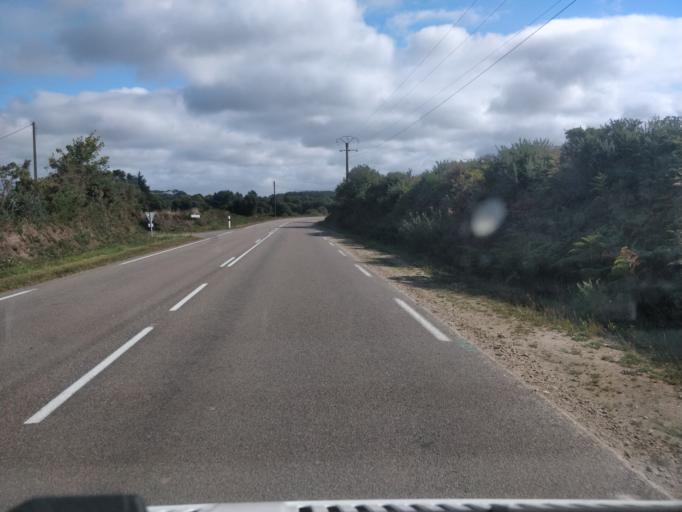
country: FR
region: Brittany
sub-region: Departement du Finistere
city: Landudec
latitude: 47.9969
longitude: -4.3759
